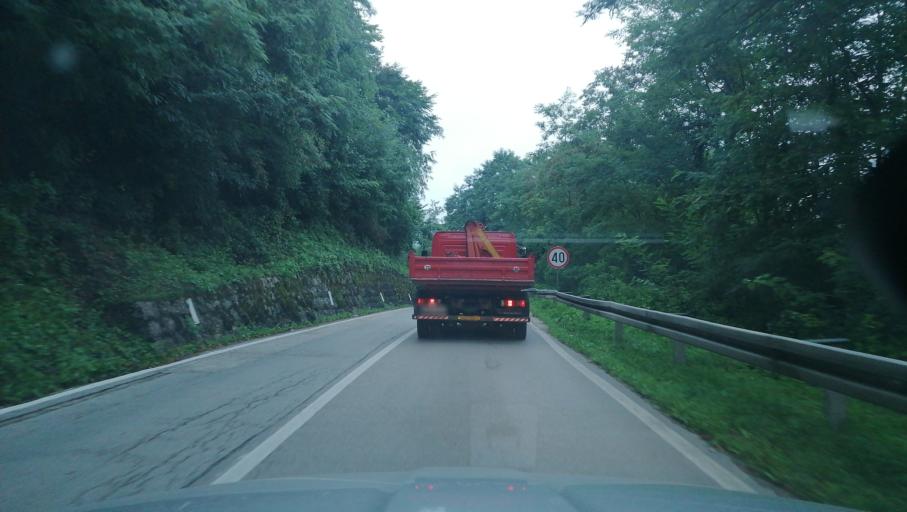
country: BA
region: Federation of Bosnia and Herzegovina
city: Jablanica
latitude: 43.7251
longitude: 17.6973
